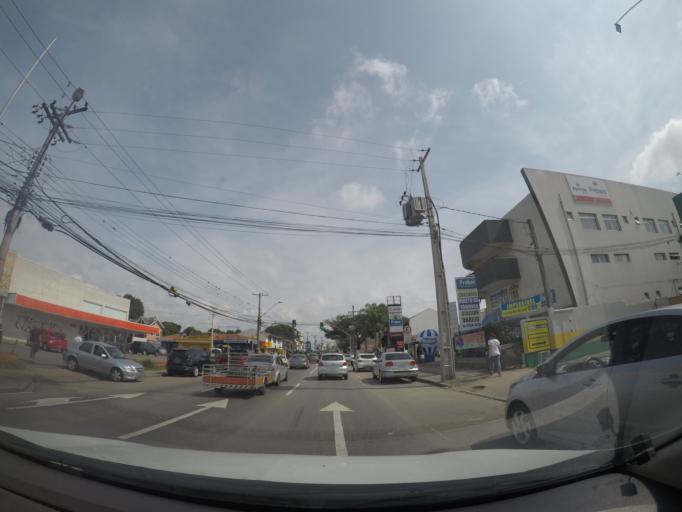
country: BR
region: Parana
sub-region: Curitiba
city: Curitiba
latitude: -25.4945
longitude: -49.2831
